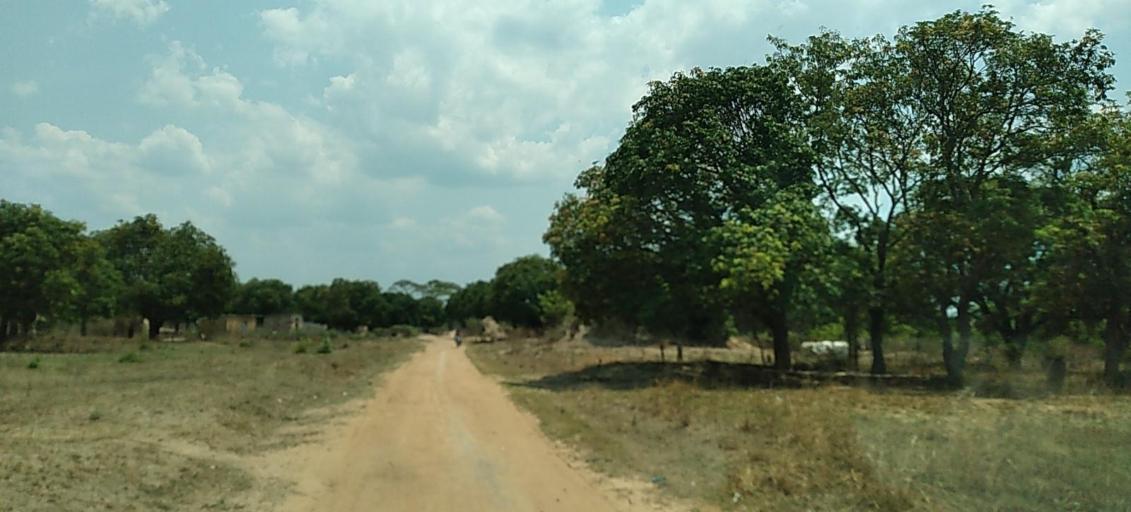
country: ZM
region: Copperbelt
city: Luanshya
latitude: -13.1620
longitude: 28.3072
